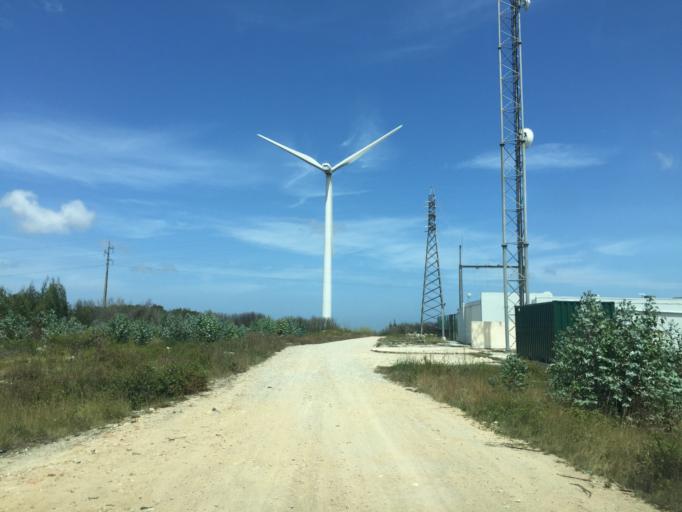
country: PT
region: Leiria
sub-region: Peniche
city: Atouguia da Baleia
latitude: 39.3210
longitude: -9.2608
